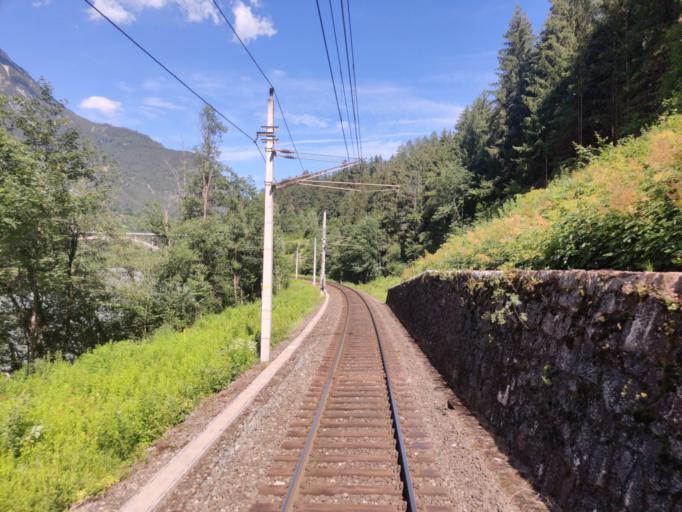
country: AT
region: Tyrol
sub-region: Politischer Bezirk Imst
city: Karrosten
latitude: 47.2159
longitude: 10.7486
